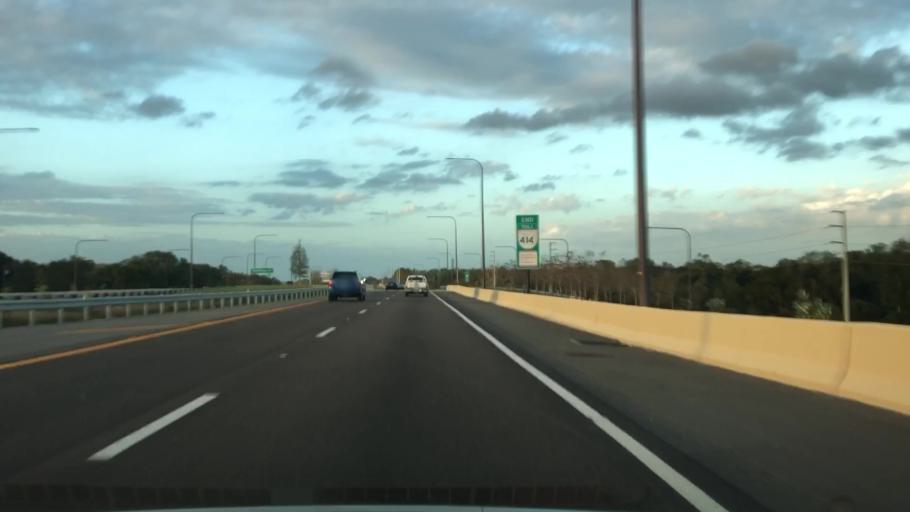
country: US
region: Florida
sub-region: Orange County
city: Apopka
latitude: 28.6991
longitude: -81.5591
